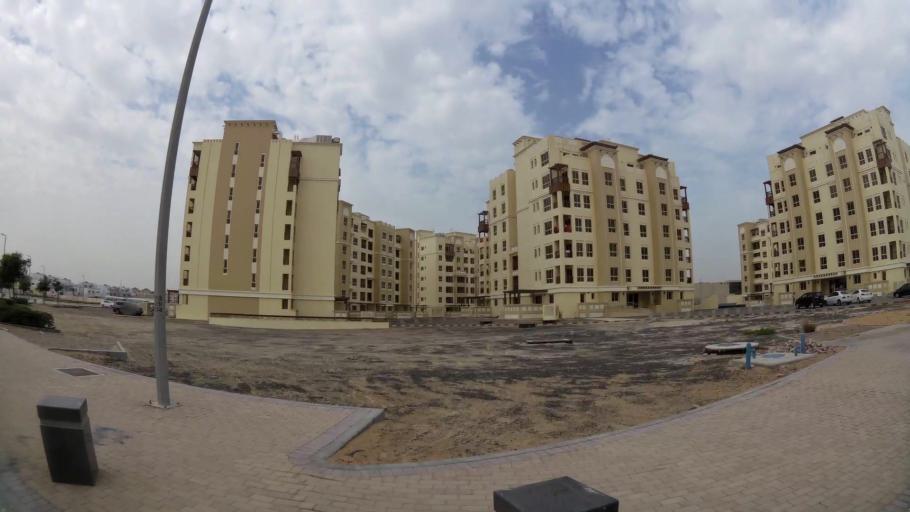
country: AE
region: Abu Dhabi
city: Abu Dhabi
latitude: 24.3108
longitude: 54.6241
